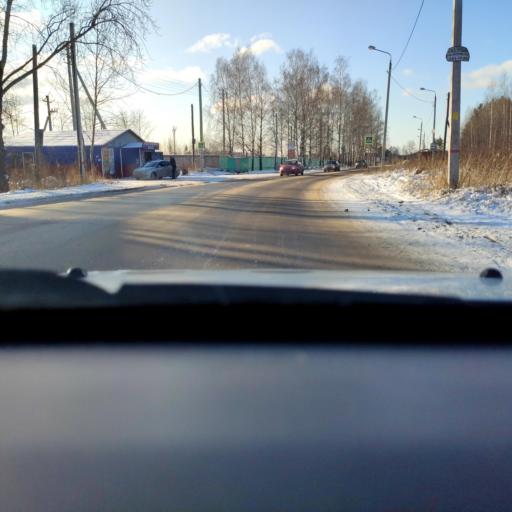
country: RU
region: Perm
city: Perm
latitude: 58.0419
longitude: 56.2704
